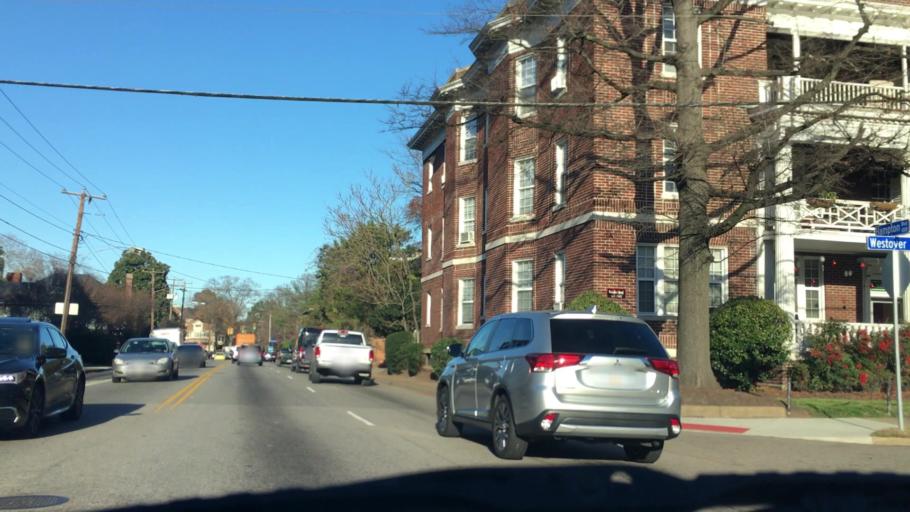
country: US
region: Virginia
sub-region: City of Norfolk
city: Norfolk
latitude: 36.8650
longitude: -76.3016
